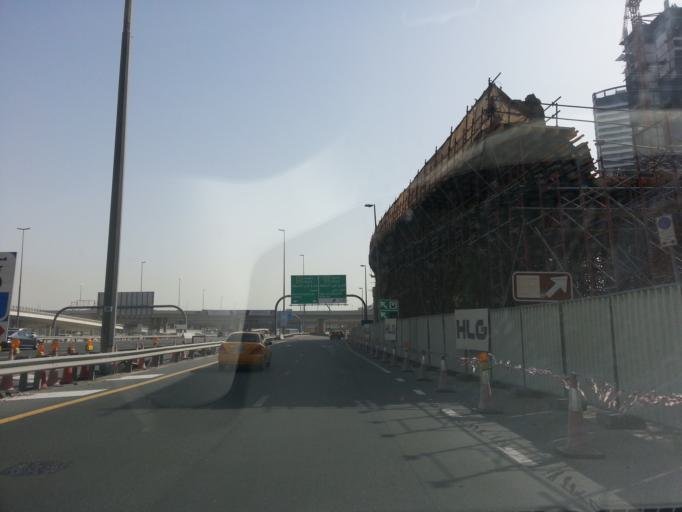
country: AE
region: Dubai
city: Dubai
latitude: 25.0693
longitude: 55.1362
